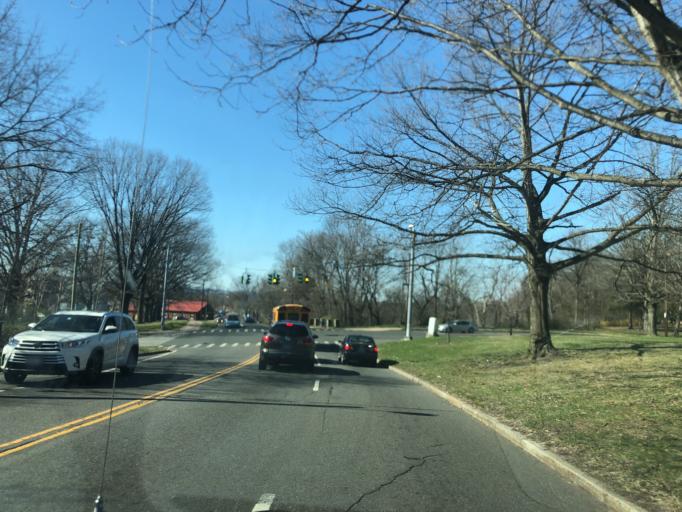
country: US
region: Connecticut
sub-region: Hartford County
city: Hartford
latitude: 41.7411
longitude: -72.6930
